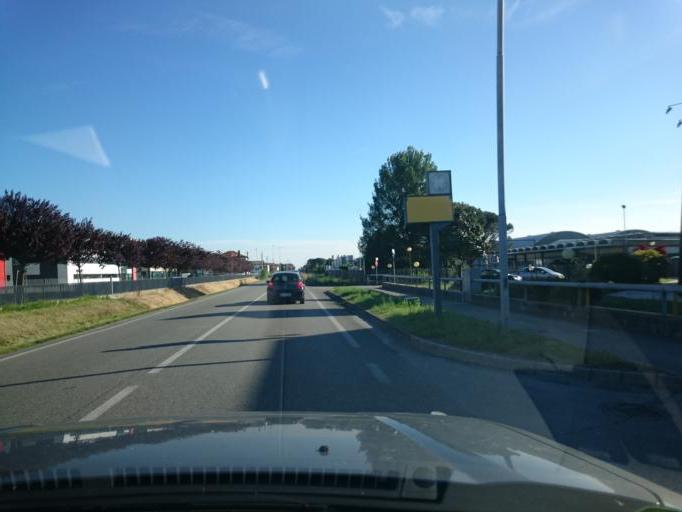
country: IT
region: Veneto
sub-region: Provincia di Venezia
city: Sant'Angelo
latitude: 45.5047
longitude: 12.0112
